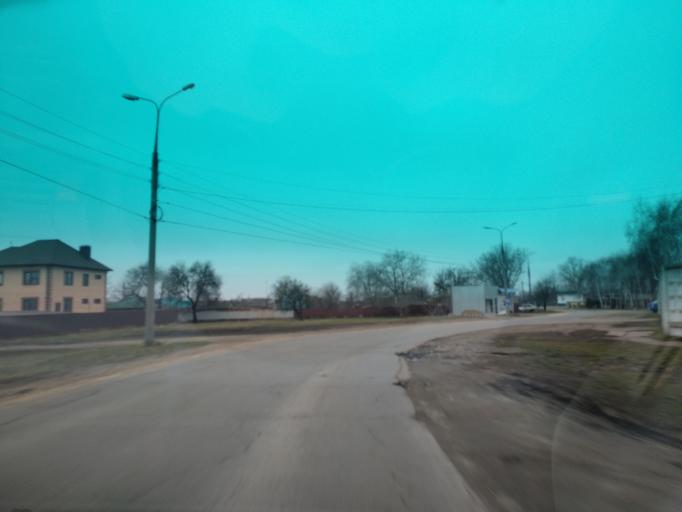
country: RU
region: Krasnodarskiy
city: Tikhoretsk
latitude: 45.8390
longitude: 40.1230
